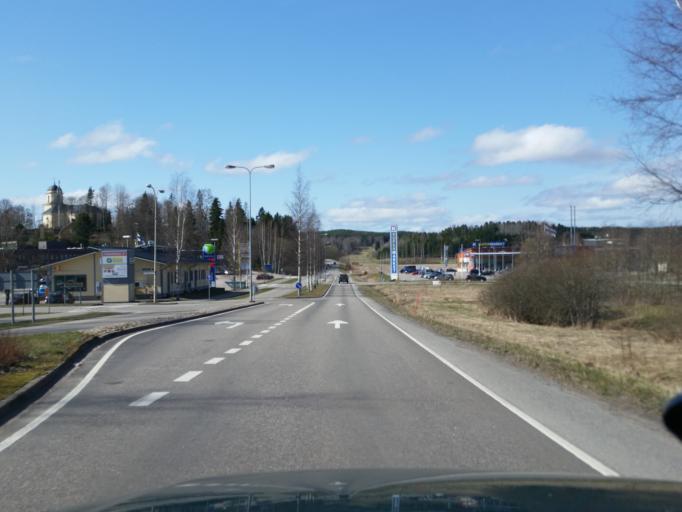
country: FI
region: Uusimaa
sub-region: Helsinki
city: Vihti
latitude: 60.4161
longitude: 24.3265
